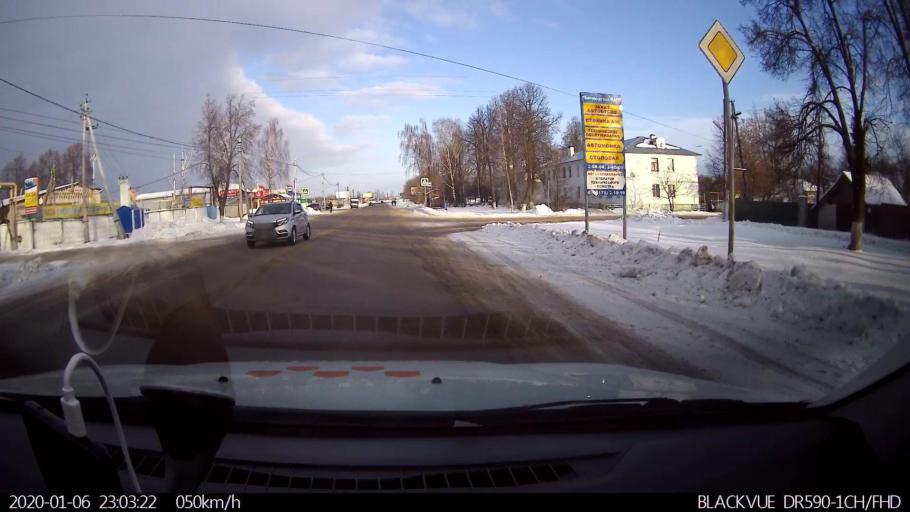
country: RU
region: Nizjnij Novgorod
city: Bogorodsk
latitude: 56.1123
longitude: 43.5334
